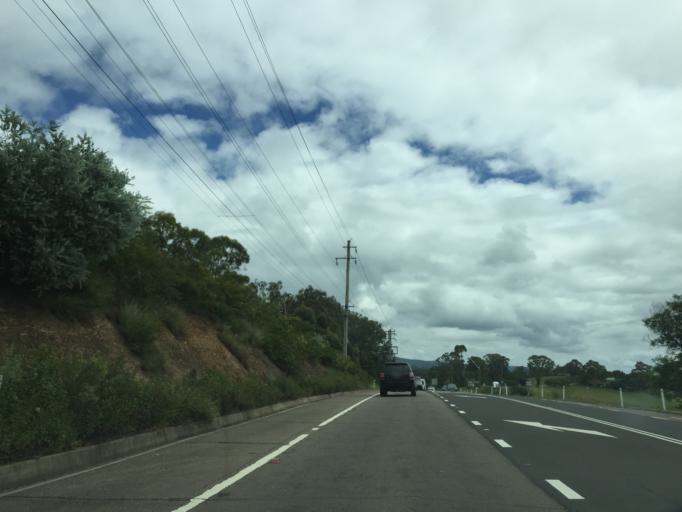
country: AU
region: New South Wales
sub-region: Hawkesbury
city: Richmond
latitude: -33.5704
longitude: 150.7059
